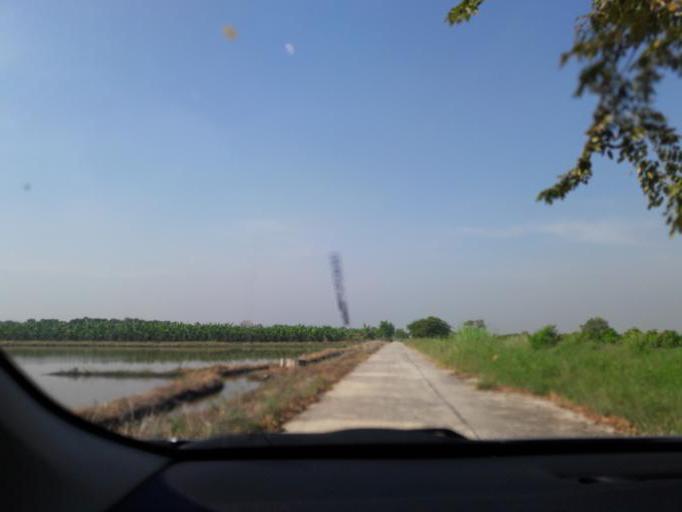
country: TH
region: Ang Thong
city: Ang Thong
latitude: 14.5916
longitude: 100.4273
